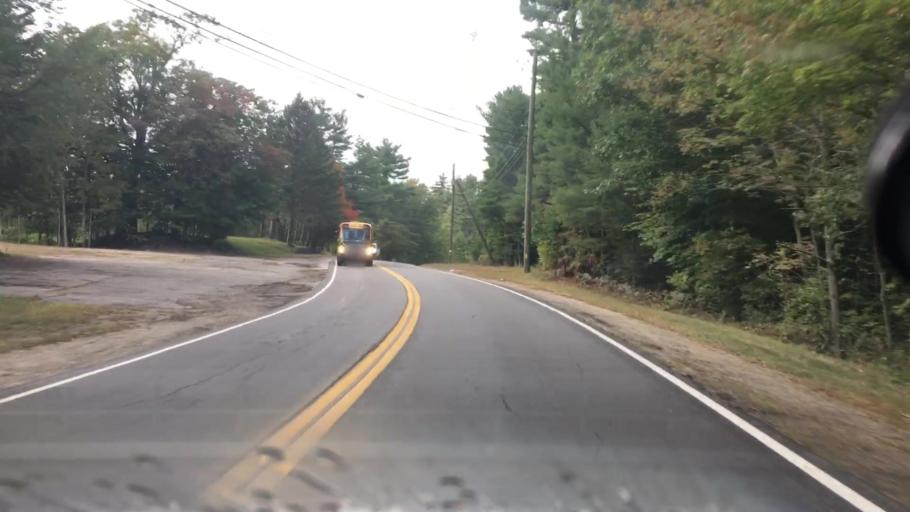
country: US
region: New Hampshire
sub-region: Carroll County
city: Wakefield
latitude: 43.5637
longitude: -71.0286
